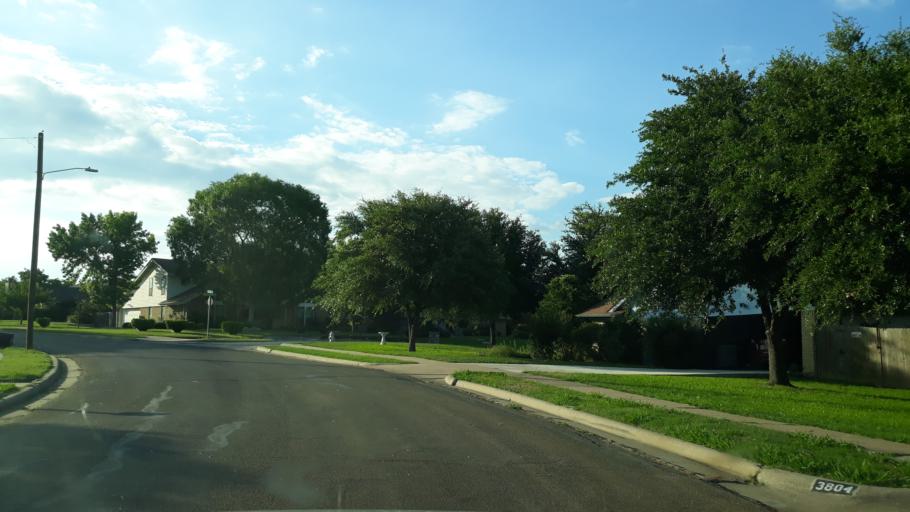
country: US
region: Texas
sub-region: Dallas County
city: Irving
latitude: 32.8609
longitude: -96.9976
